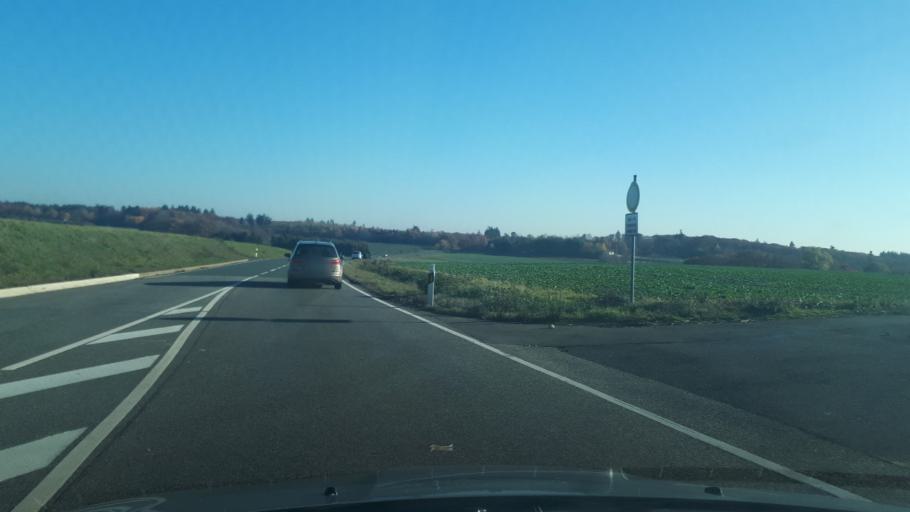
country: DE
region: Rheinland-Pfalz
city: Buchel
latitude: 50.1702
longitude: 7.0875
